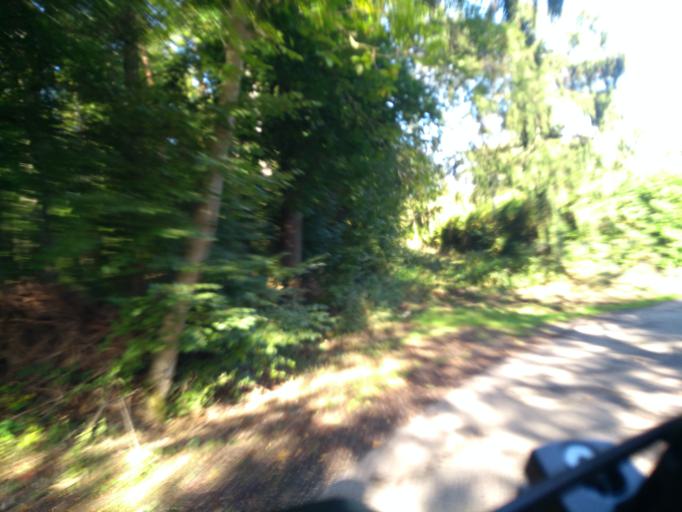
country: DE
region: Baden-Wuerttemberg
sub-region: Karlsruhe Region
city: Birkenfeld
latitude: 48.8963
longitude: 8.6405
